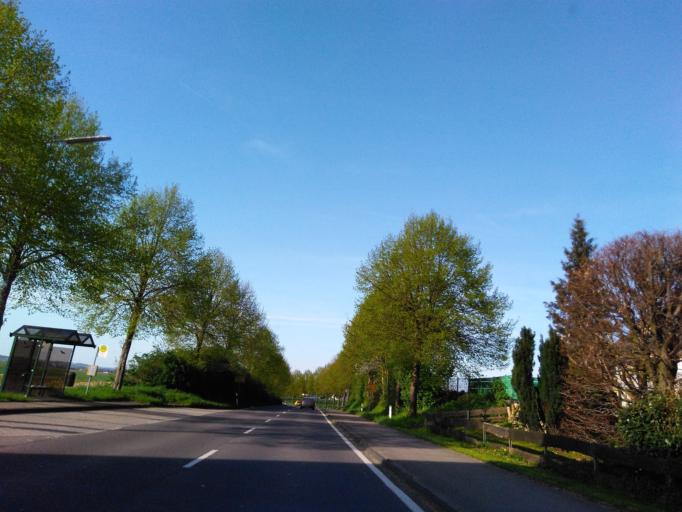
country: DE
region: North Rhine-Westphalia
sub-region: Regierungsbezirk Koln
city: Hennef
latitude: 50.8346
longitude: 7.2859
